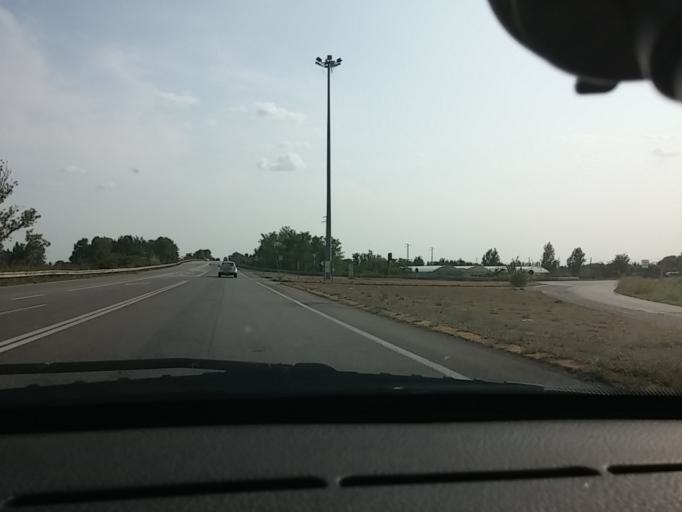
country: IT
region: Emilia-Romagna
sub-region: Provincia di Ferrara
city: Gaibanella-Sant'Edigio
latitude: 44.8059
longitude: 11.6361
